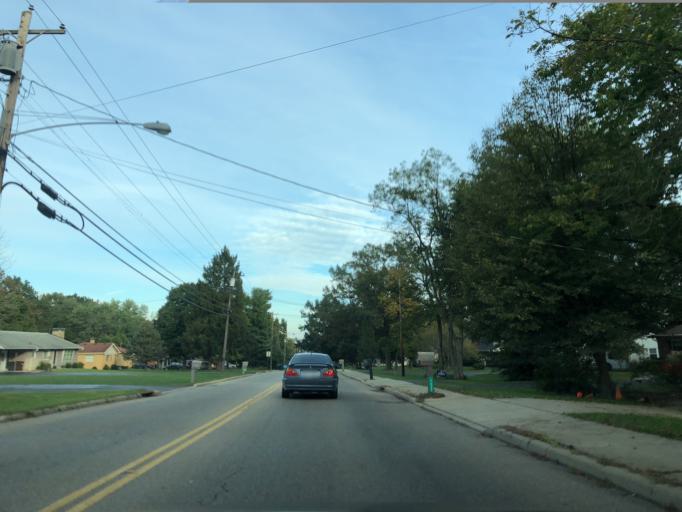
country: US
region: Ohio
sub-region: Hamilton County
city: Loveland
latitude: 39.2716
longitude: -84.2820
